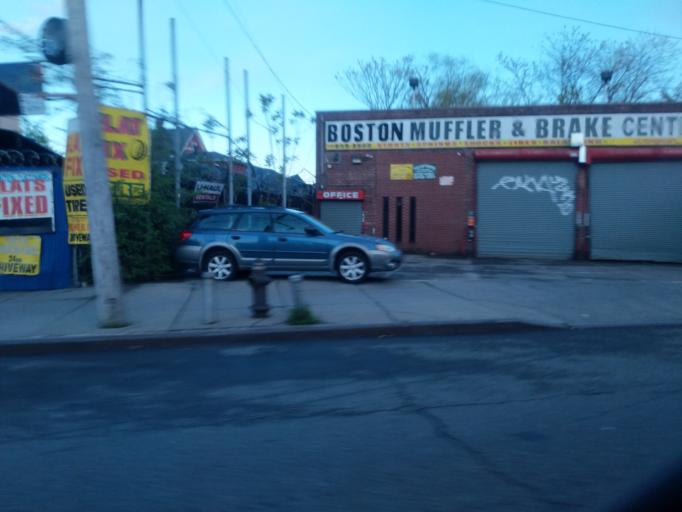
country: US
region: New York
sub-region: Bronx
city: Eastchester
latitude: 40.8787
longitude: -73.8438
